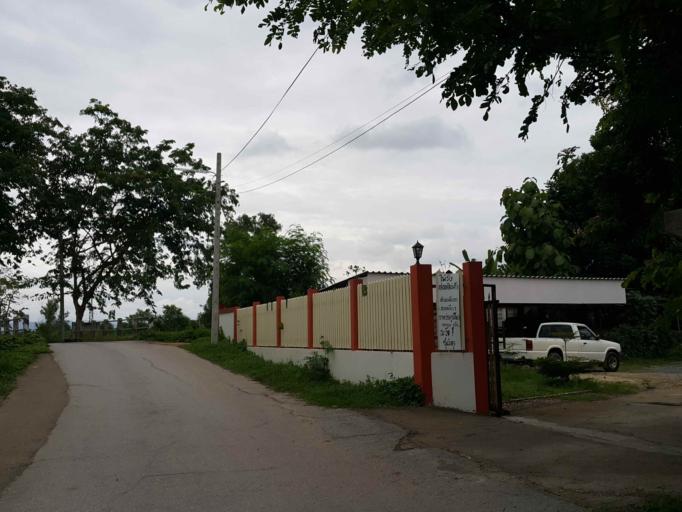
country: TH
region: Chiang Mai
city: San Sai
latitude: 18.8279
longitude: 99.0606
